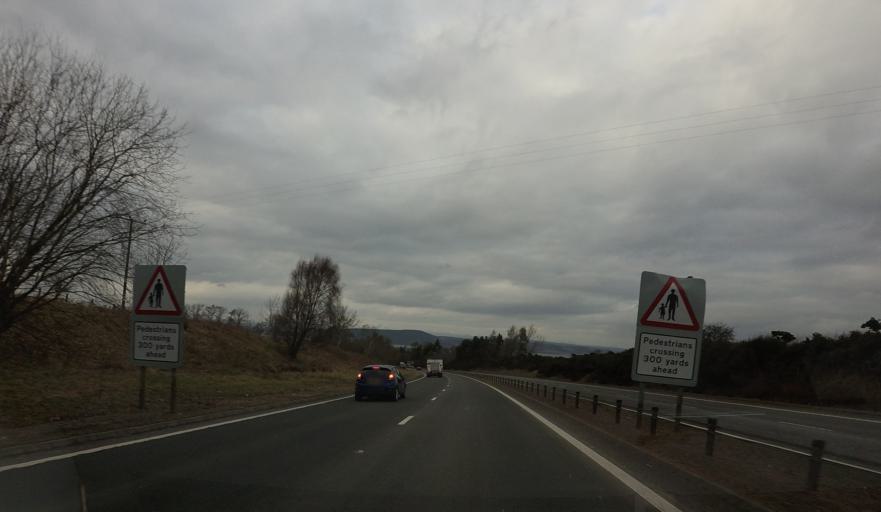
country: GB
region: Scotland
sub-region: Highland
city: Inverness
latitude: 57.4615
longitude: -4.1685
